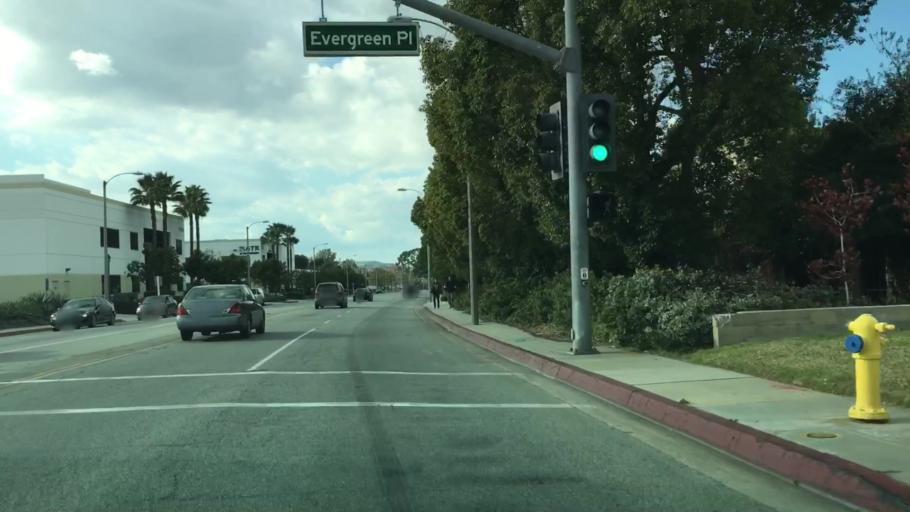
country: US
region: California
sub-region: Los Angeles County
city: La Puente
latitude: 34.0008
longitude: -117.9349
